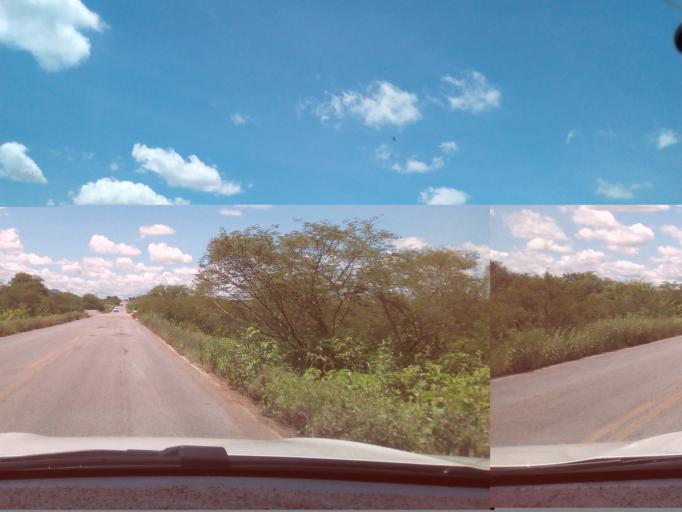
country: BR
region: Rio Grande do Norte
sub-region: Caico
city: Caico
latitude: -6.5008
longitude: -37.0779
